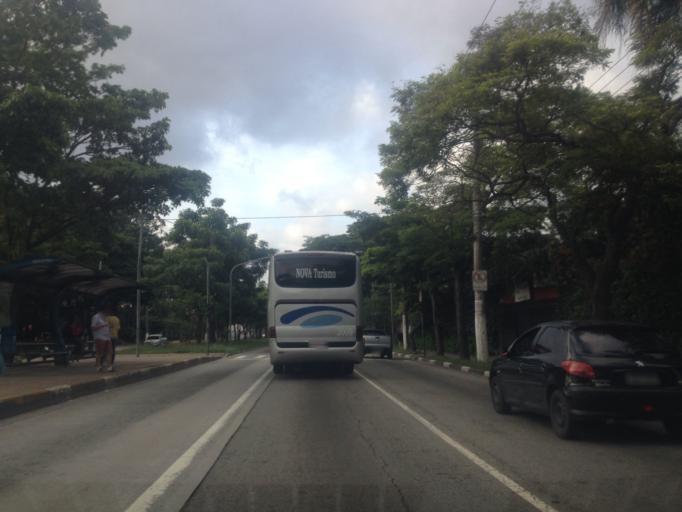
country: BR
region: Sao Paulo
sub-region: Diadema
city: Diadema
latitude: -23.6886
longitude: -46.7145
